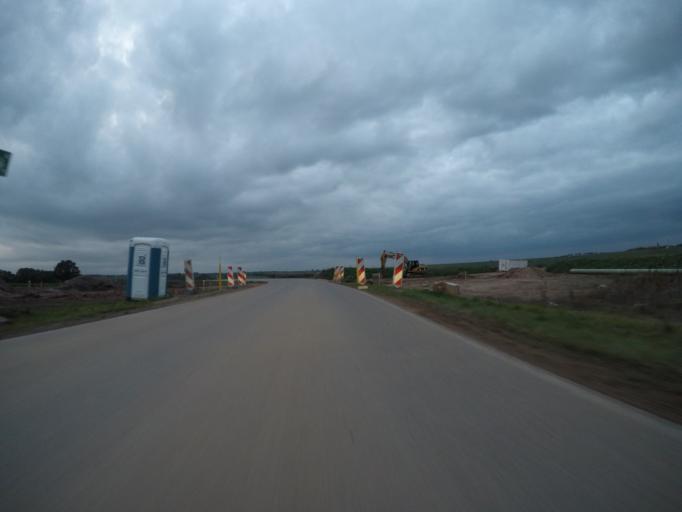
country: DE
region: Thuringia
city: Saara
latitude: 50.9193
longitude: 12.4005
